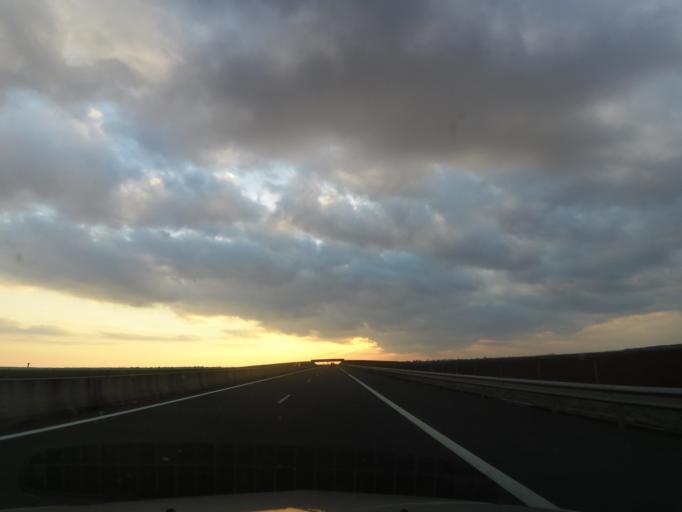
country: FR
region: Centre
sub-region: Departement du Loiret
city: Ascheres-le-Marche
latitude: 48.0903
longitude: 2.0091
